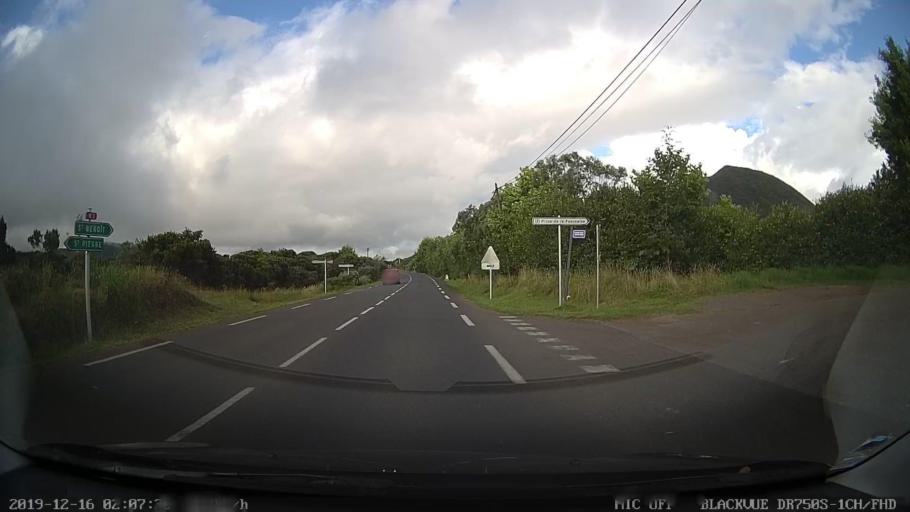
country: RE
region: Reunion
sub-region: Reunion
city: Cilaos
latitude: -21.1781
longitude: 55.5799
